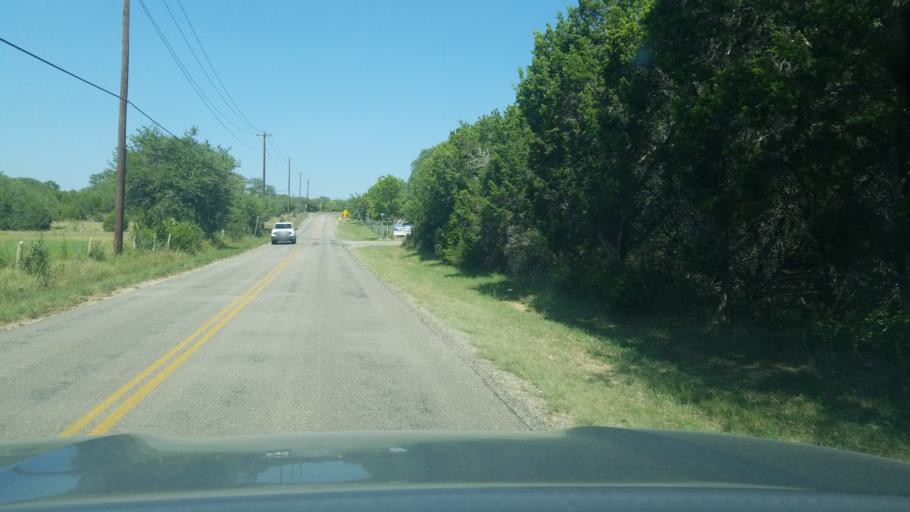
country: US
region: Texas
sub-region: Comal County
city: Bulverde
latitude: 29.7693
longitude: -98.5161
